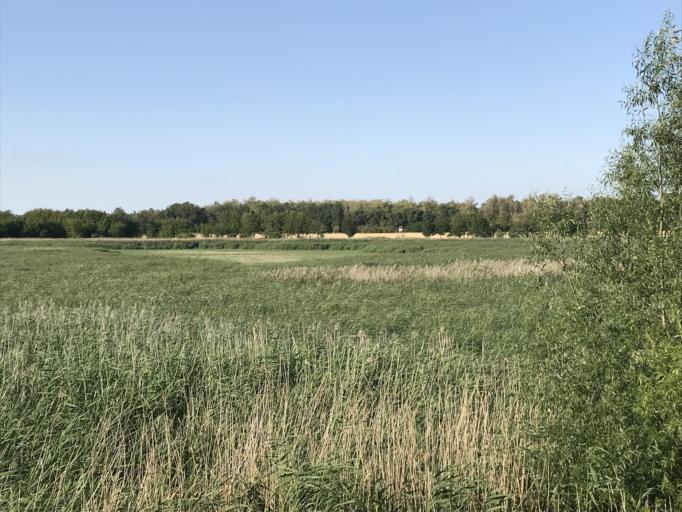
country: DE
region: Saxony-Anhalt
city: Frose
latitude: 51.8005
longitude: 11.3901
